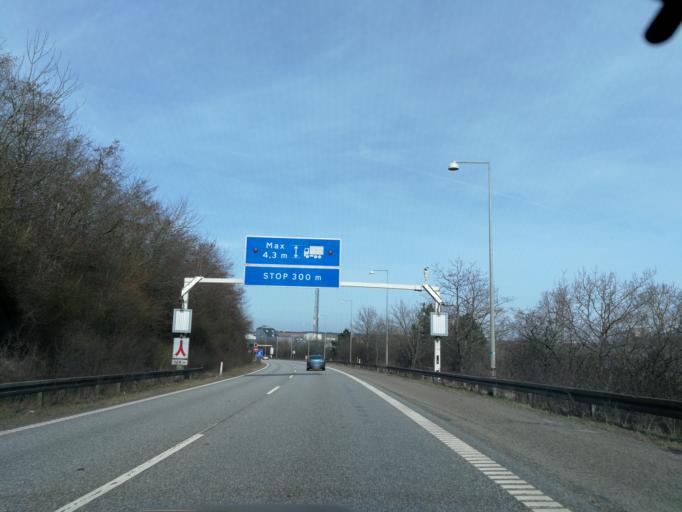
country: DK
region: North Denmark
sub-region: Alborg Kommune
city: Aalborg
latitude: 57.0501
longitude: 9.9701
